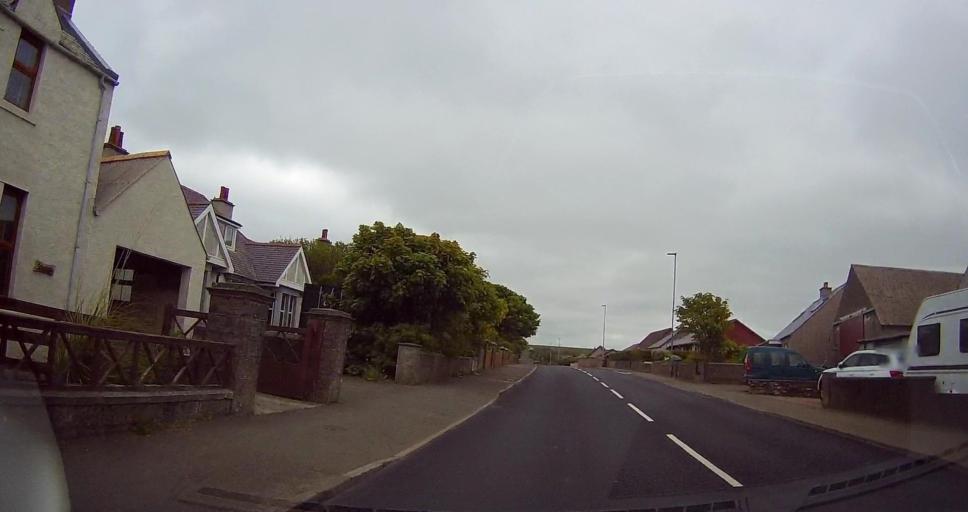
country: GB
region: Scotland
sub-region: Orkney Islands
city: Kirkwall
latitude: 58.9750
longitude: -2.9526
